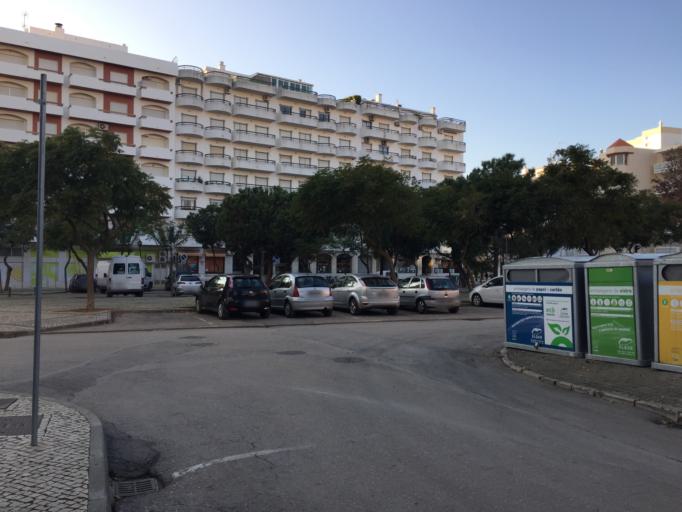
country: PT
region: Faro
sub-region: Vila Real de Santo Antonio
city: Monte Gordo
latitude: 37.1809
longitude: -7.4488
